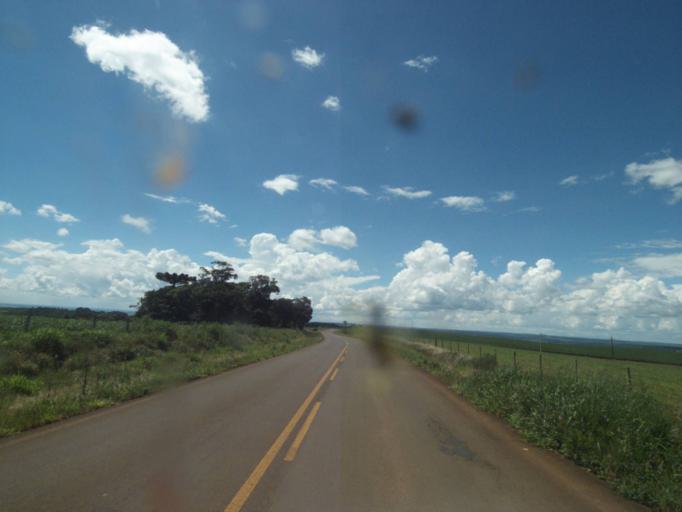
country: BR
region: Parana
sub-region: Pinhao
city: Pinhao
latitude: -25.8047
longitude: -52.0727
